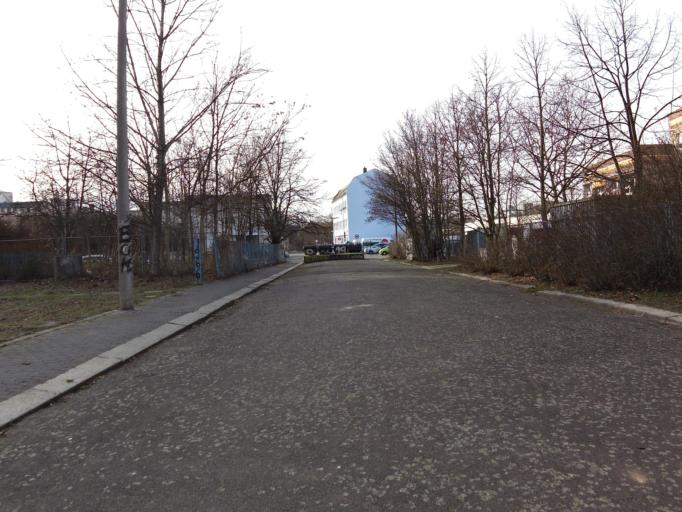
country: DE
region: Saxony
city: Leipzig
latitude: 51.3419
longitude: 12.3969
